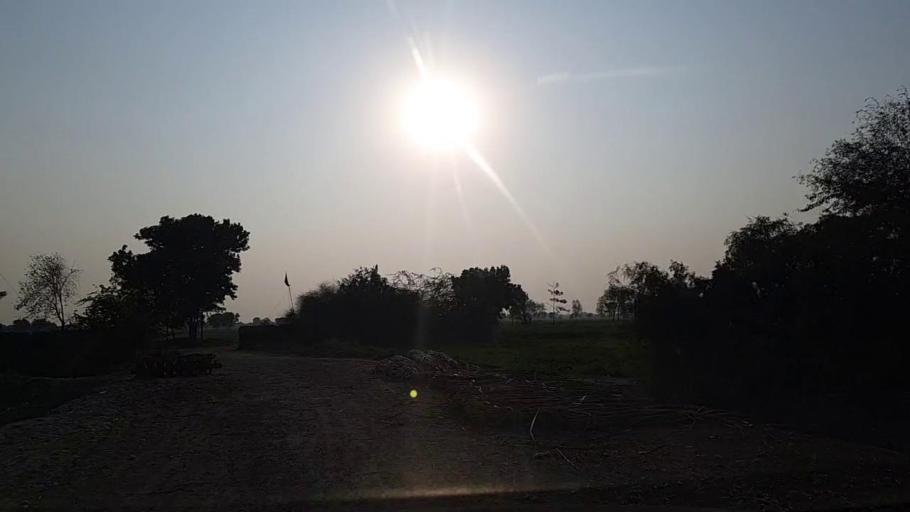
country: PK
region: Sindh
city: Daur
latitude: 26.4102
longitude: 68.3807
